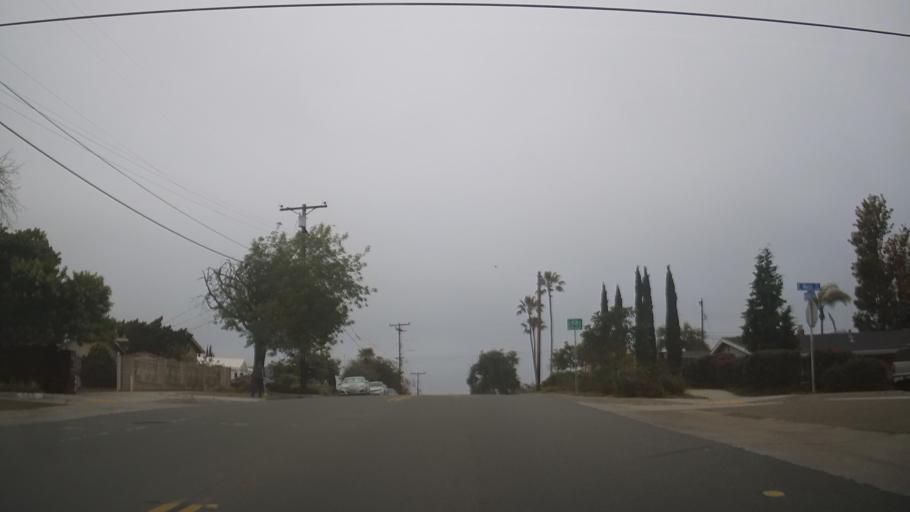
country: US
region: California
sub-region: San Diego County
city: Bonita
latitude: 32.6238
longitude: -117.0481
